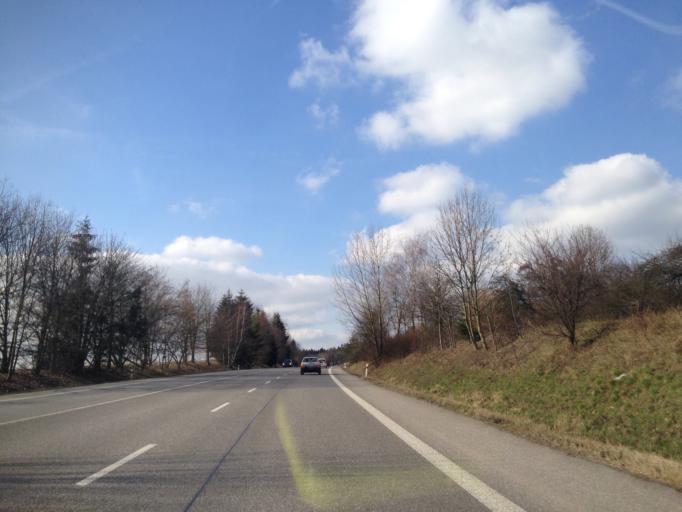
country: CZ
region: Kralovehradecky
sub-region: Okres Jicin
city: Sobotka
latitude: 50.4571
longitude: 15.2185
